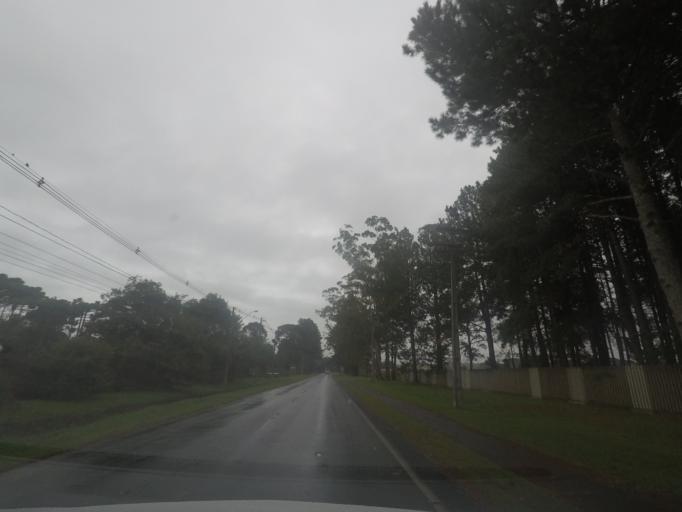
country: BR
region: Parana
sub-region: Quatro Barras
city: Quatro Barras
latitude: -25.3734
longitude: -49.0906
